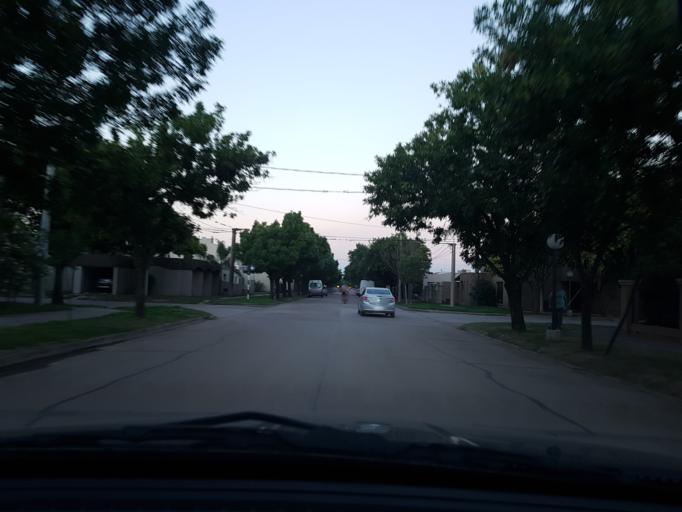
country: AR
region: Cordoba
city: General Cabrera
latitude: -32.7598
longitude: -63.7972
